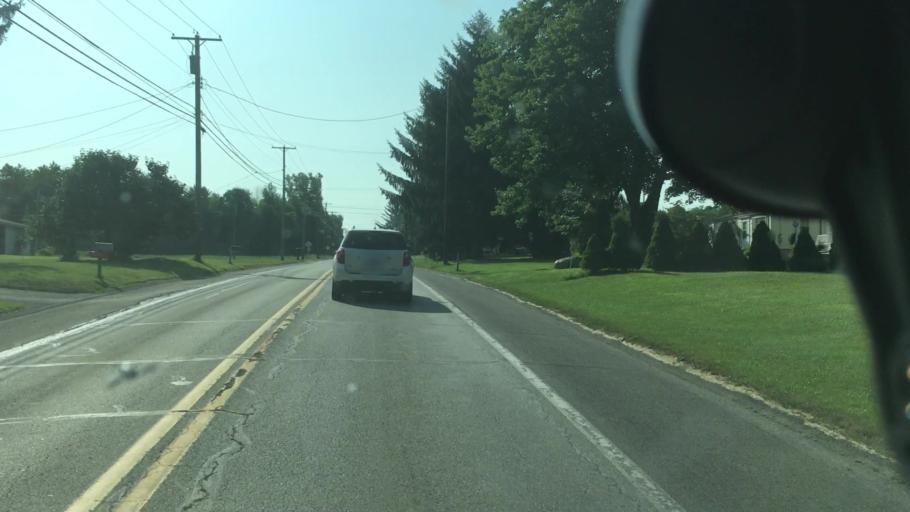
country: US
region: Pennsylvania
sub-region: Lawrence County
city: Oakwood
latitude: 41.0193
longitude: -80.4152
